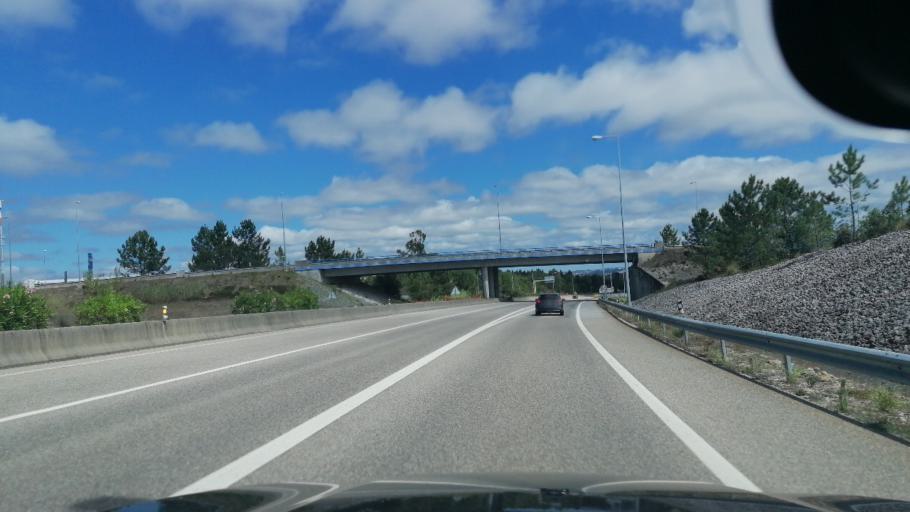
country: PT
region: Leiria
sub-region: Leiria
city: Maceira
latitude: 39.7427
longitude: -8.8735
